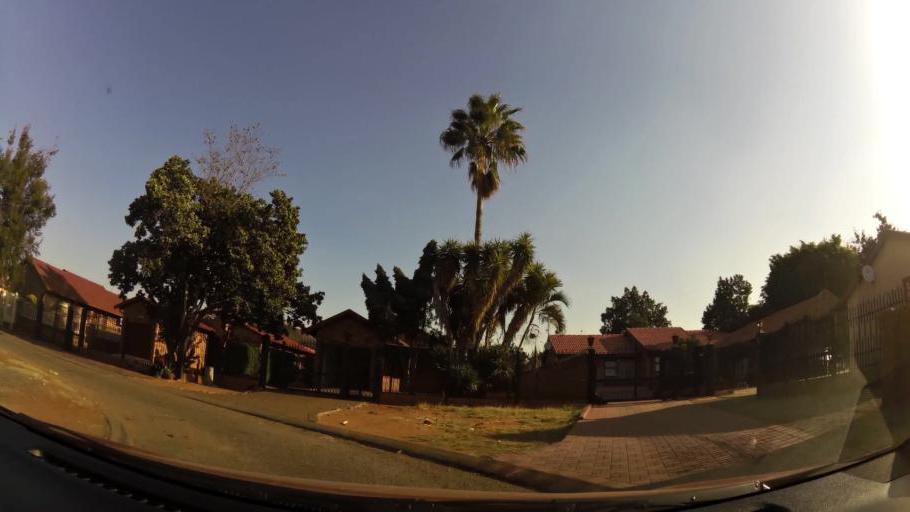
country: ZA
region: North-West
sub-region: Bojanala Platinum District Municipality
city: Rustenburg
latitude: -25.6511
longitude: 27.2180
